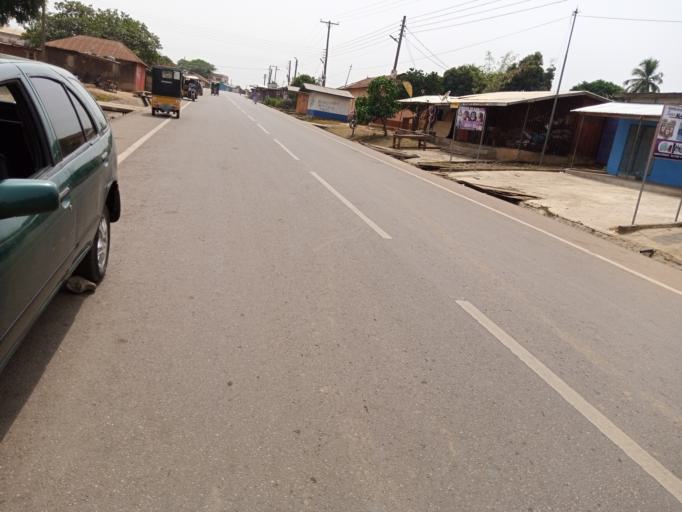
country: GH
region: Volta
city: Kpandu
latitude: 7.0053
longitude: 0.2956
